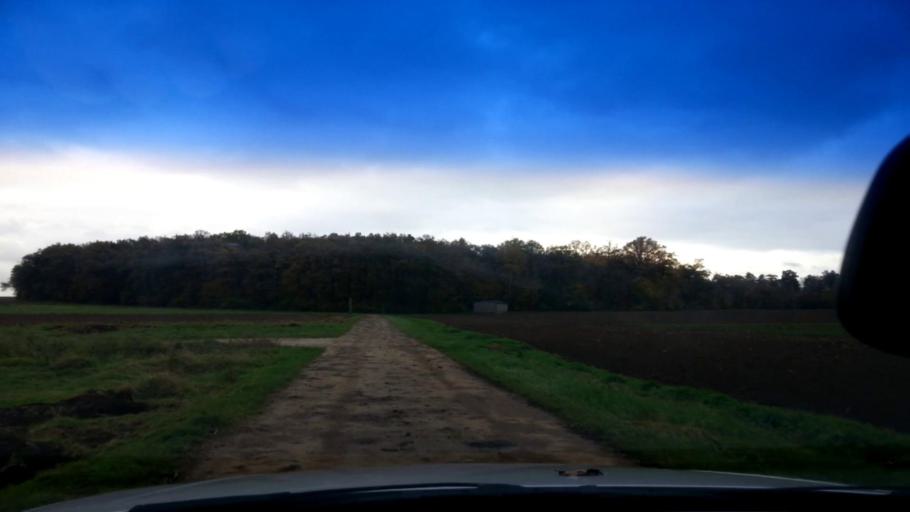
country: DE
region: Bavaria
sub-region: Upper Franconia
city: Gundelsheim
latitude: 49.9559
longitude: 10.9422
